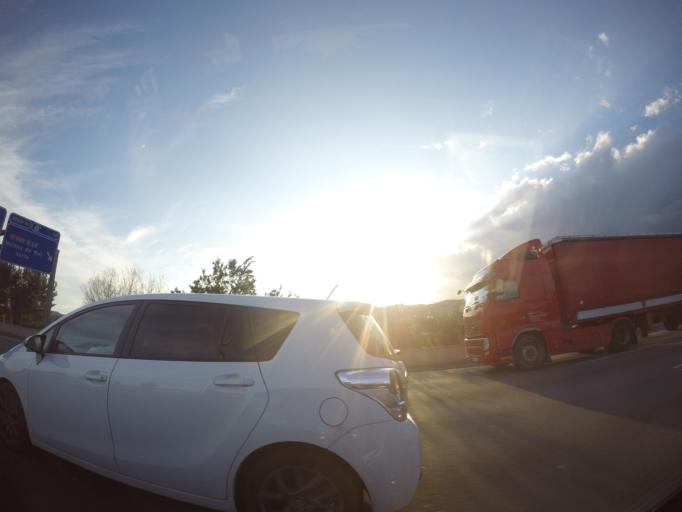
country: ES
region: Catalonia
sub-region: Provincia de Barcelona
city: Palleja
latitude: 41.4369
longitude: 2.0022
